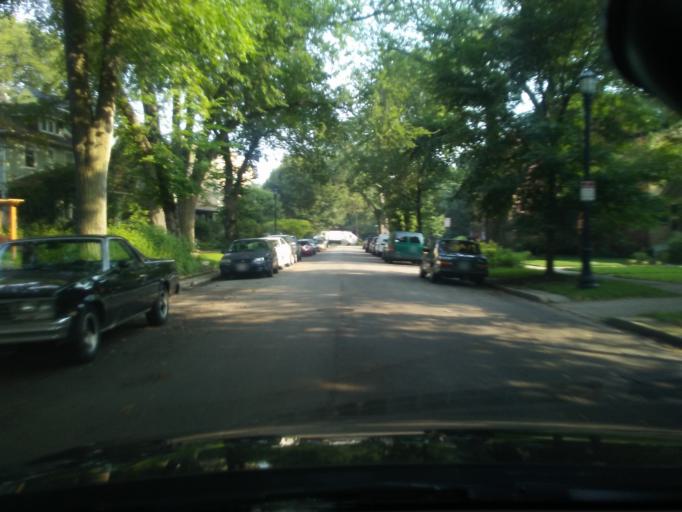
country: US
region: Illinois
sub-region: Cook County
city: Evanston
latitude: 42.0385
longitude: -87.6864
